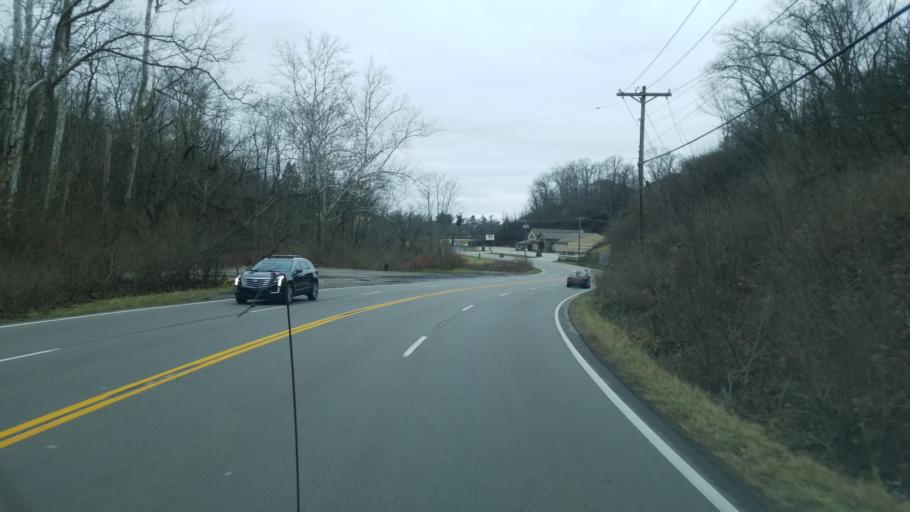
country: US
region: Kentucky
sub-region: Campbell County
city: Fort Thomas
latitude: 39.0642
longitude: -84.4582
